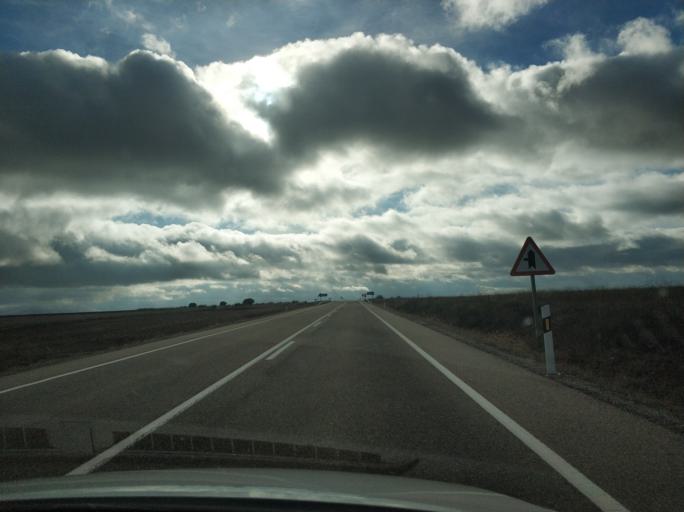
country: ES
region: Castille and Leon
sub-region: Provincia de Soria
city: Fuentecambron
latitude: 41.4626
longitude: -3.3301
